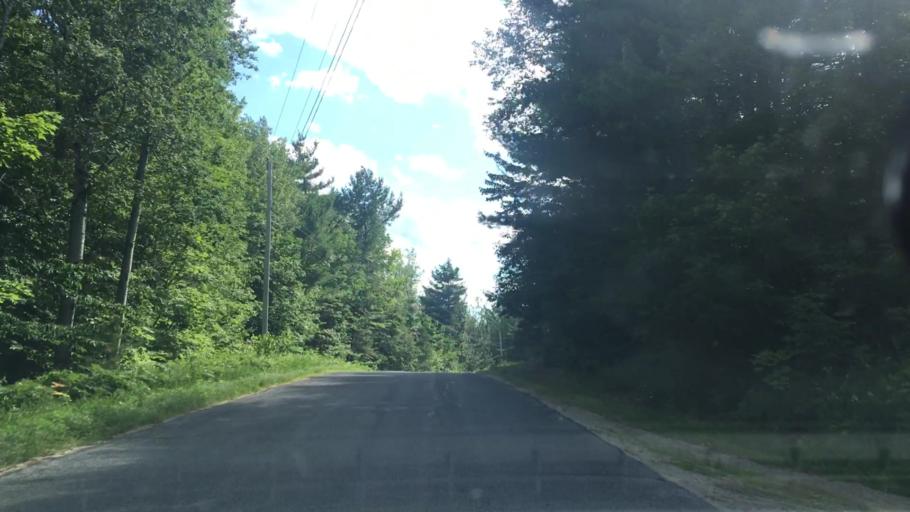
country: US
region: Maine
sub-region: Franklin County
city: Wilton
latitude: 44.6239
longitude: -70.2137
